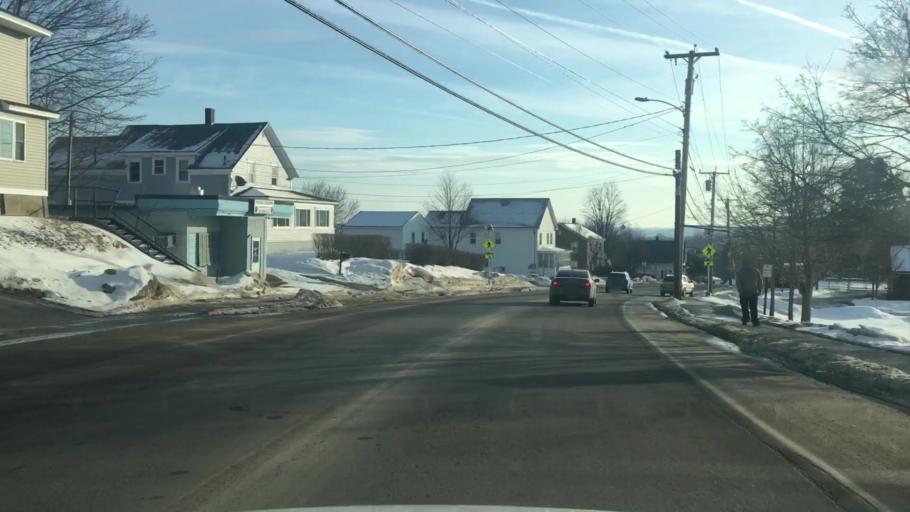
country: US
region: Maine
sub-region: Kennebec County
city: Augusta
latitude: 44.3305
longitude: -69.7765
